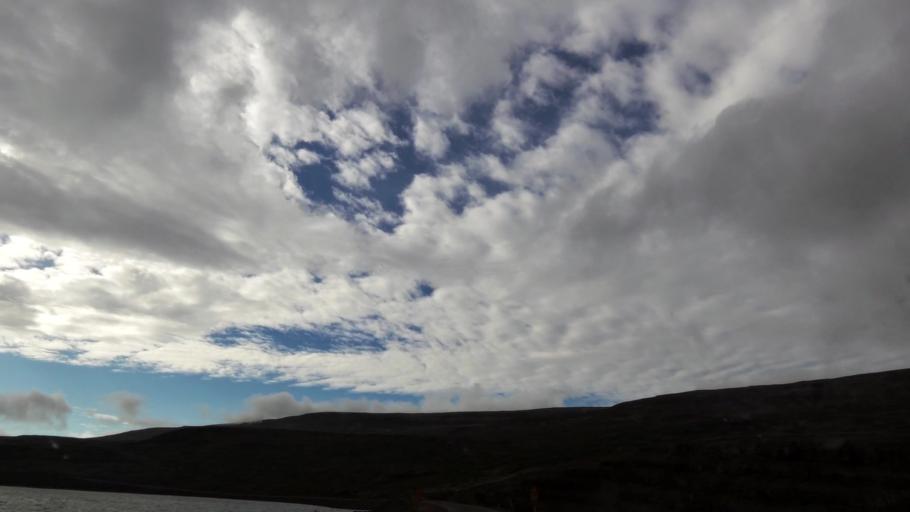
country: IS
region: West
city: Olafsvik
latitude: 65.5361
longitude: -23.7871
